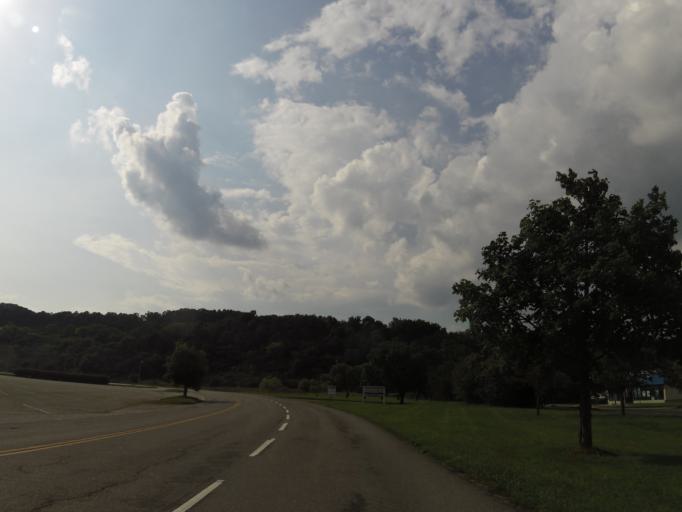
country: US
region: Tennessee
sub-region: Knox County
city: Knoxville
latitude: 36.0354
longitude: -83.8733
